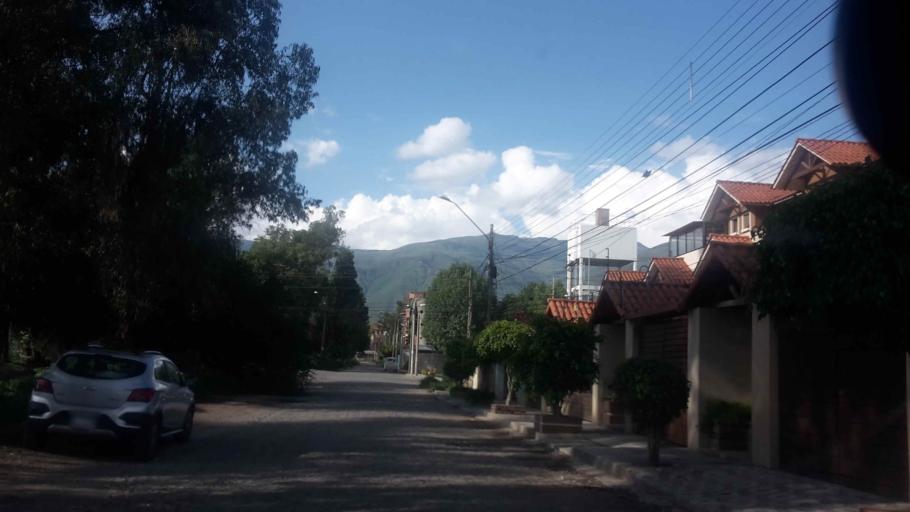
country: BO
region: Cochabamba
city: Cochabamba
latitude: -17.3786
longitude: -66.1960
